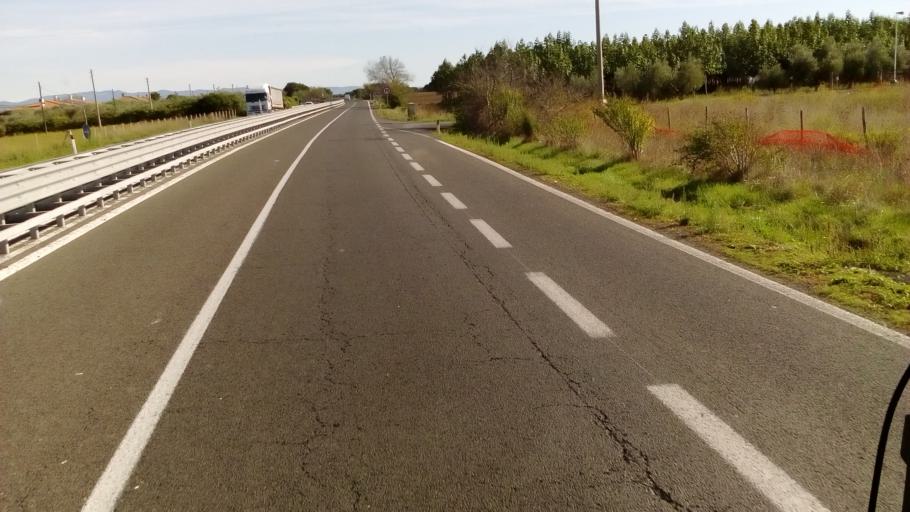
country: IT
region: Latium
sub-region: Provincia di Viterbo
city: Montalto di Castro
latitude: 42.3289
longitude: 11.6311
